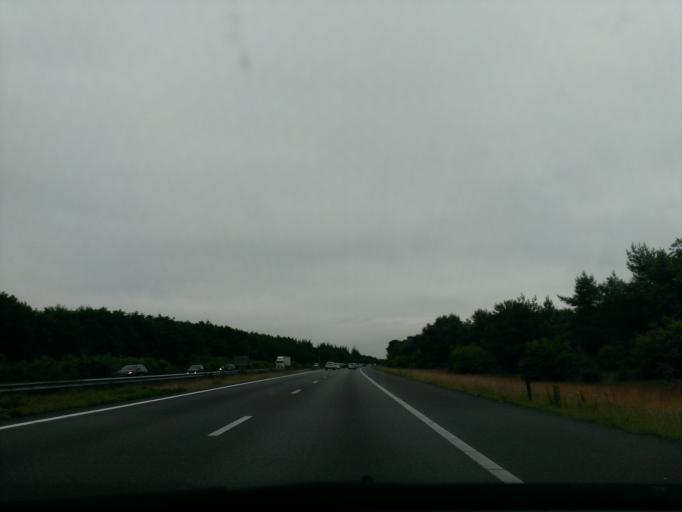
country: NL
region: Gelderland
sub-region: Gemeente Hattem
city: Hattem
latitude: 52.4573
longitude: 6.0331
